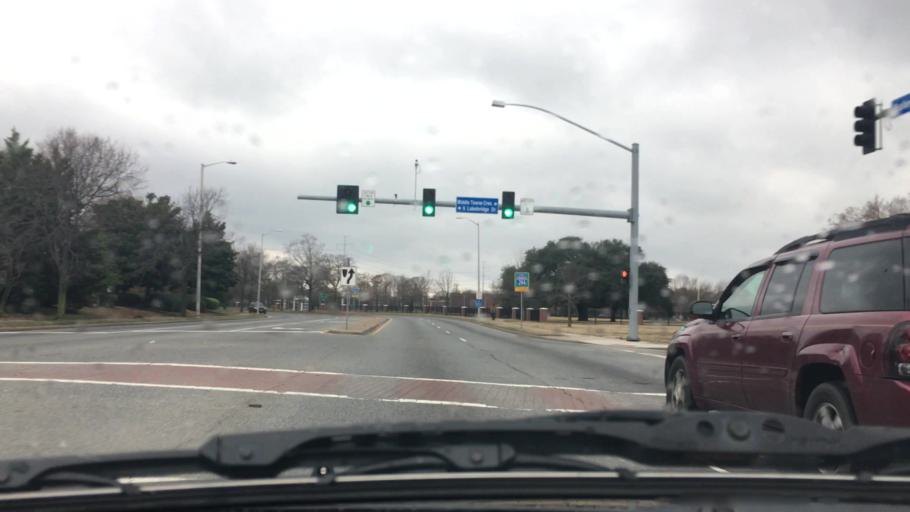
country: US
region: Virginia
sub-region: City of Norfolk
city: Norfolk
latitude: 36.8482
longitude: -76.2510
